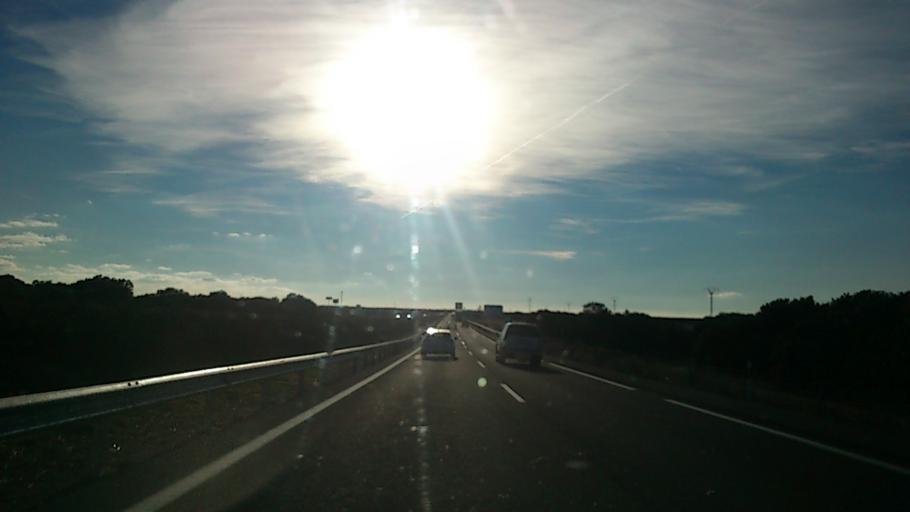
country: ES
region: Castille-La Mancha
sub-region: Provincia de Guadalajara
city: Mirabueno
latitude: 40.9365
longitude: -2.7054
